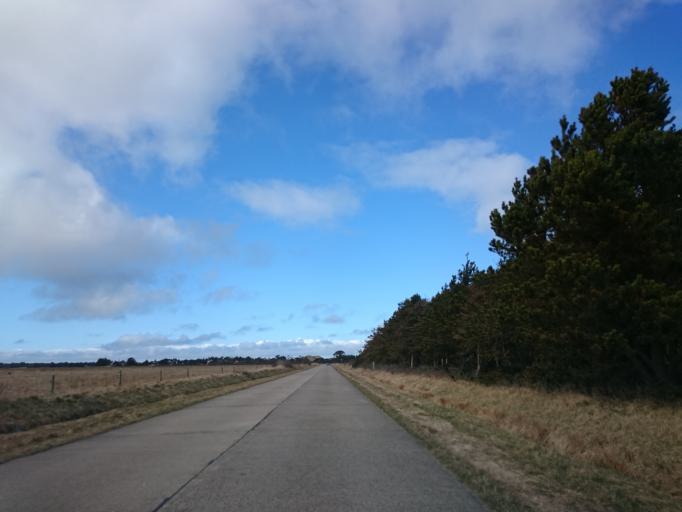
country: DK
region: North Denmark
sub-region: Frederikshavn Kommune
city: Skagen
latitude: 57.6594
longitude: 10.4041
